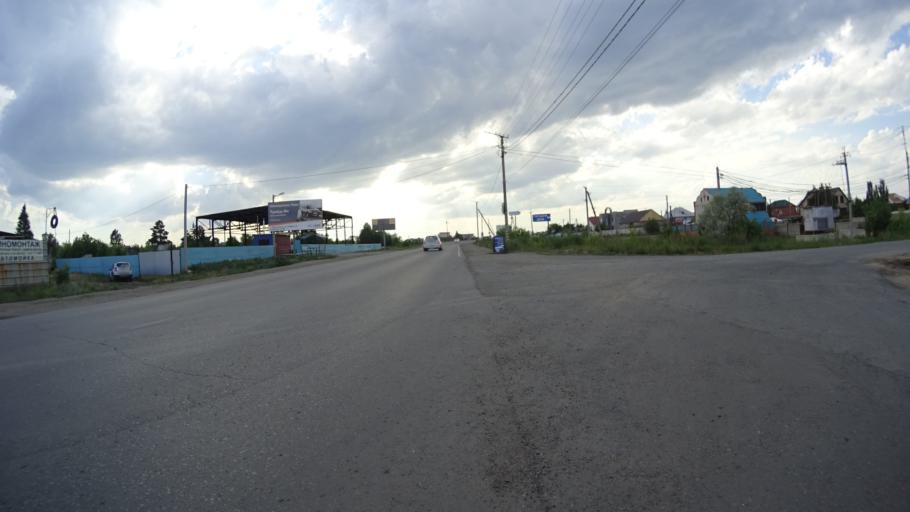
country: RU
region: Chelyabinsk
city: Troitsk
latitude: 54.0841
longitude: 61.5072
